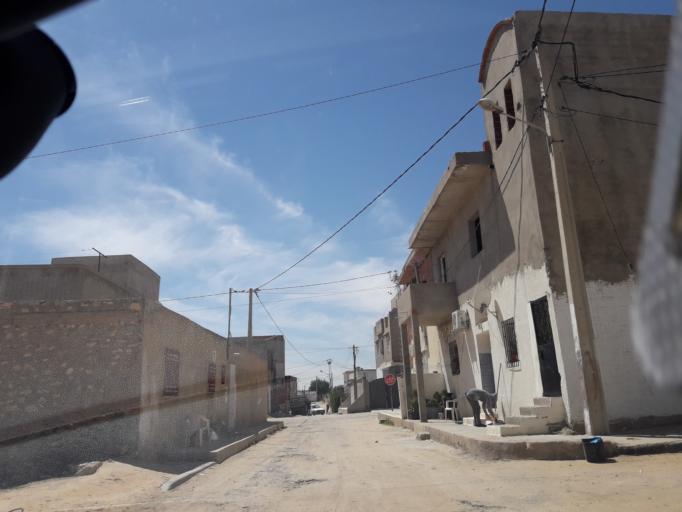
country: TN
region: Safaqis
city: Sfax
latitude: 34.7379
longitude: 10.5233
